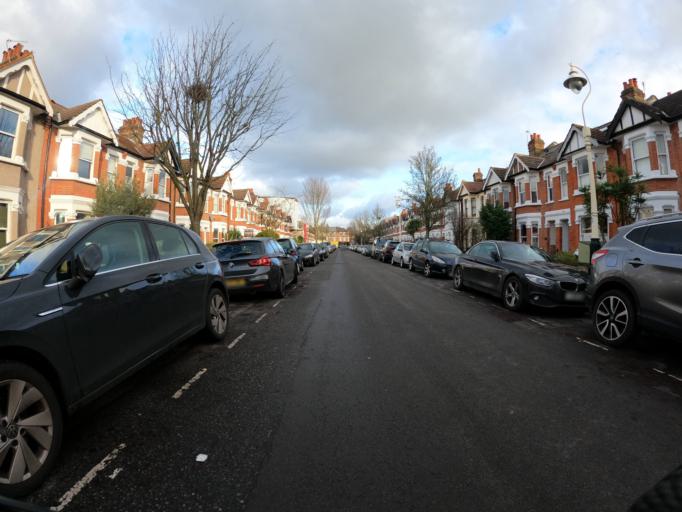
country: GB
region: England
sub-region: Greater London
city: Brentford
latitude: 51.5014
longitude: -0.3189
